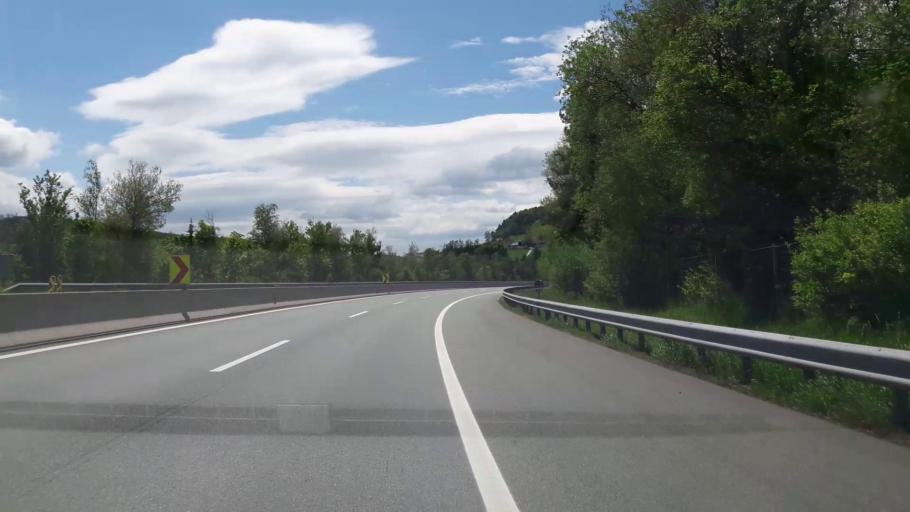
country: AT
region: Styria
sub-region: Politischer Bezirk Hartberg-Fuerstenfeld
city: Schaeffern
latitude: 47.4461
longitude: 16.0988
